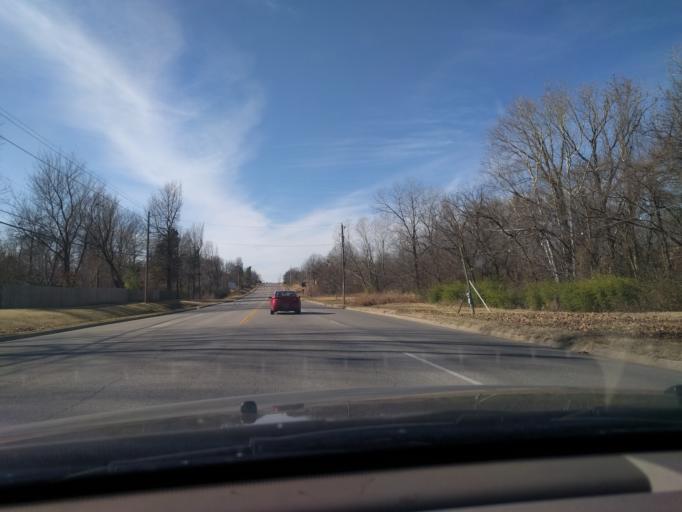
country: US
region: Oklahoma
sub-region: Tulsa County
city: Broken Arrow
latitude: 36.0608
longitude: -95.7136
